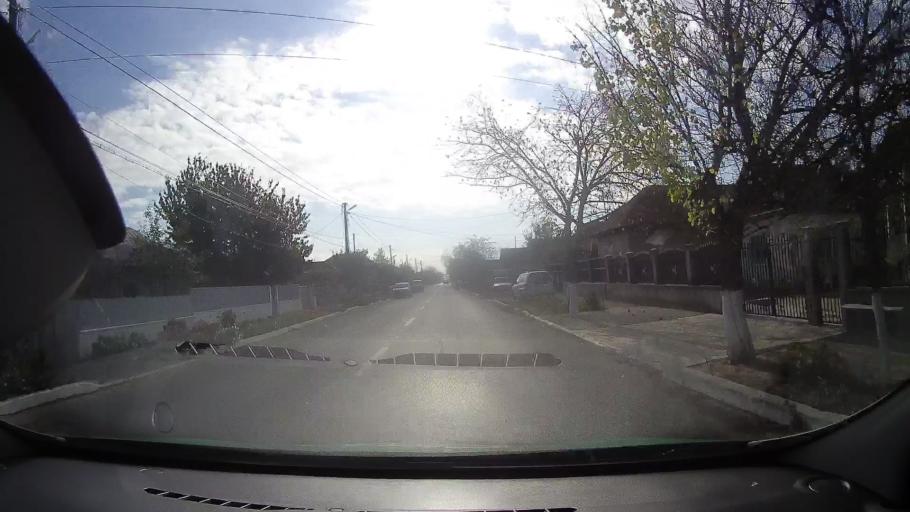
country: RO
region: Tulcea
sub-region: Comuna Sarichioi
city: Sarichioi
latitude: 44.9488
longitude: 28.8520
